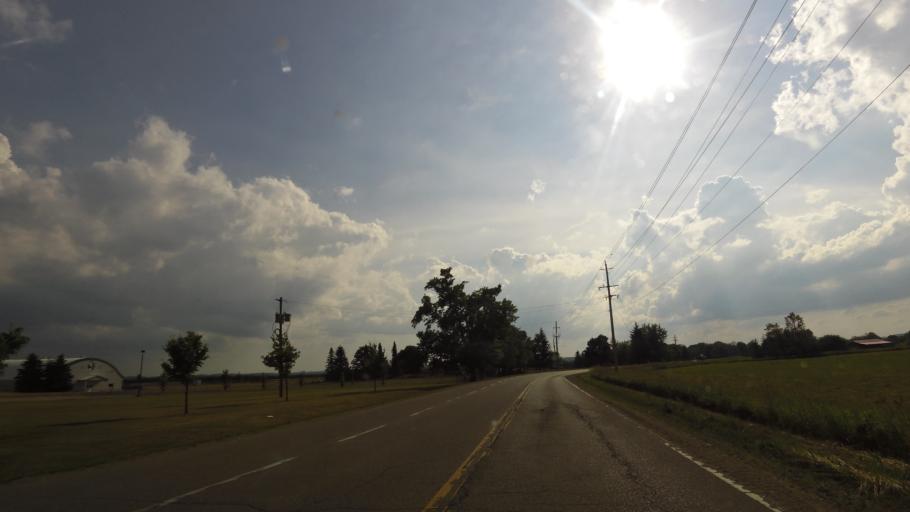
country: CA
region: Ontario
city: Orangeville
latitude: 43.9512
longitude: -80.0776
